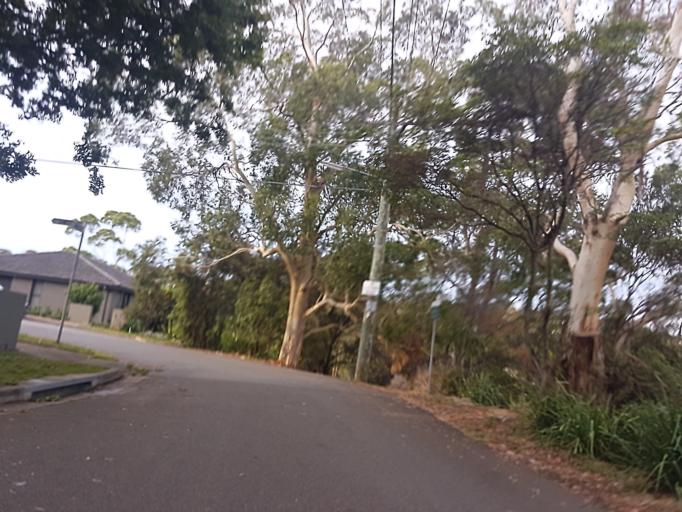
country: AU
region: New South Wales
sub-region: North Sydney
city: Cammeray
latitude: -33.8167
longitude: 151.2089
